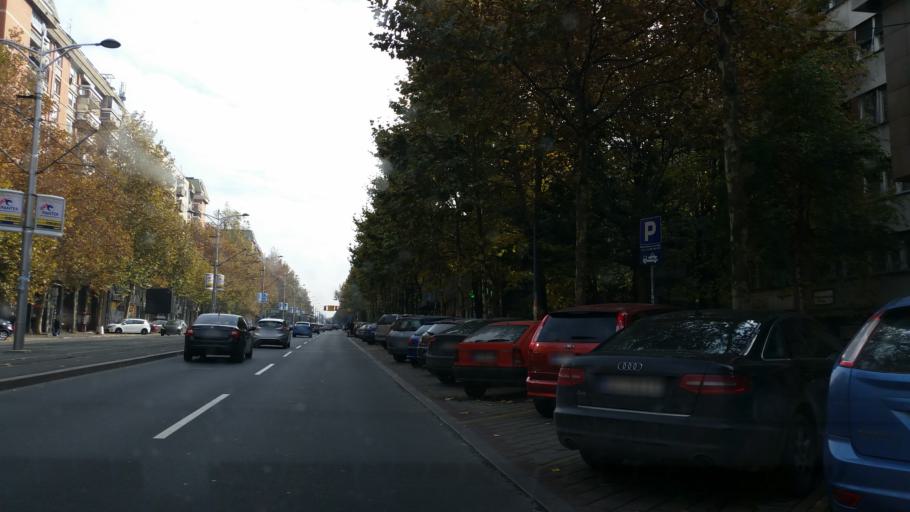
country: RS
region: Central Serbia
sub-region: Belgrade
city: Vracar
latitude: 44.7966
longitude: 20.4964
